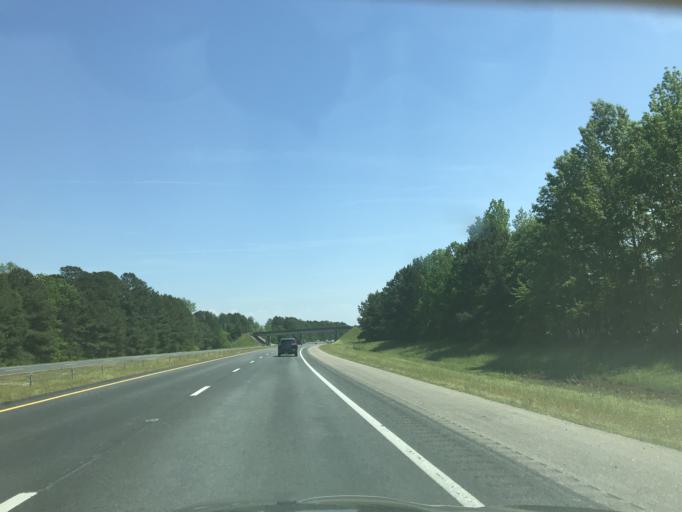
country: US
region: North Carolina
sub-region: Johnston County
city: Benson
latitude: 35.3426
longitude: -78.4690
